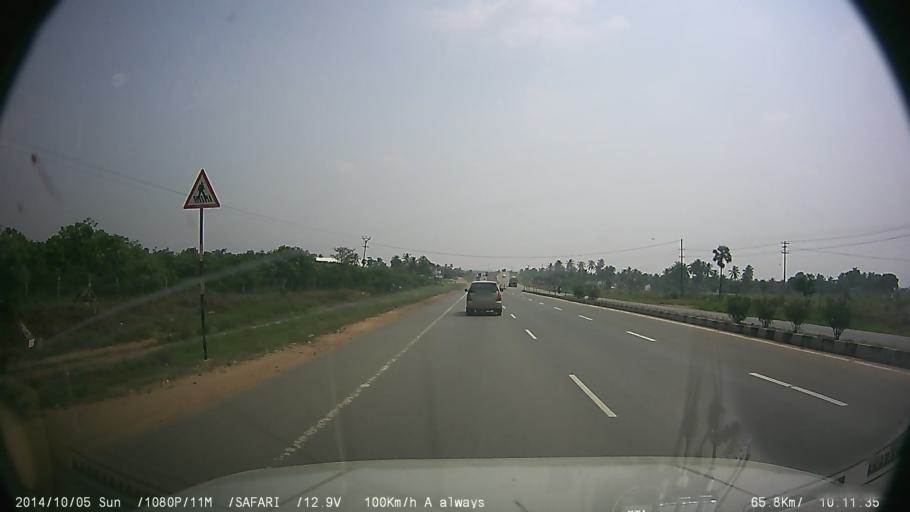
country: IN
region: Tamil Nadu
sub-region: Salem
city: Konganapuram
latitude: 11.5410
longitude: 77.9747
